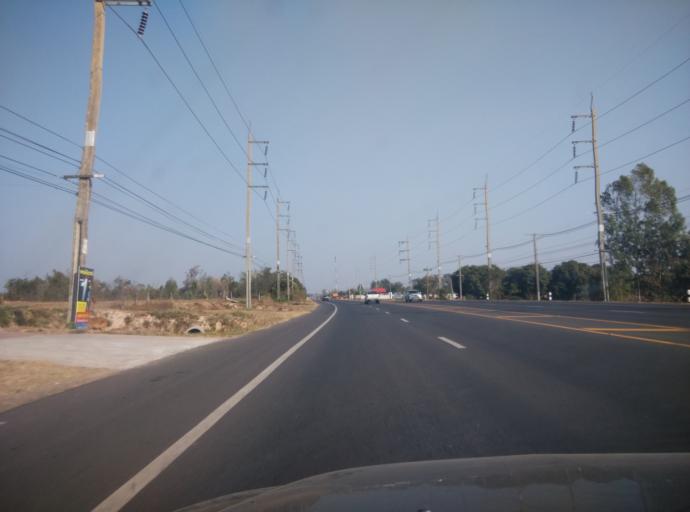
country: TH
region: Sisaket
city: Uthumphon Phisai
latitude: 15.1583
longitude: 104.1761
